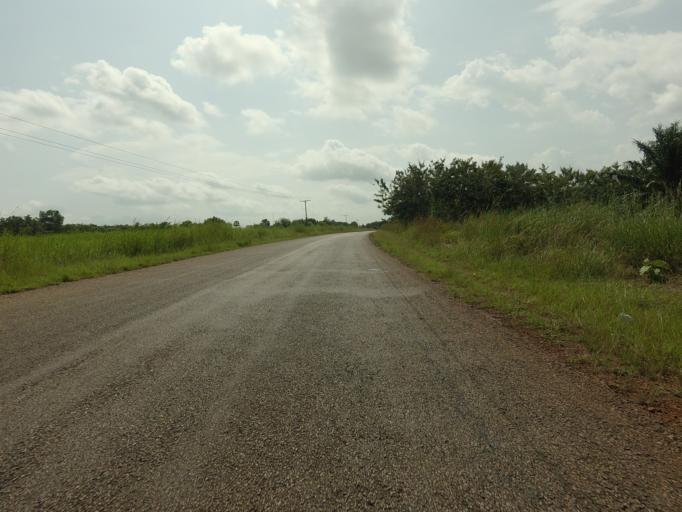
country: TG
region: Maritime
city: Lome
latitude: 6.2605
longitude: 0.9580
